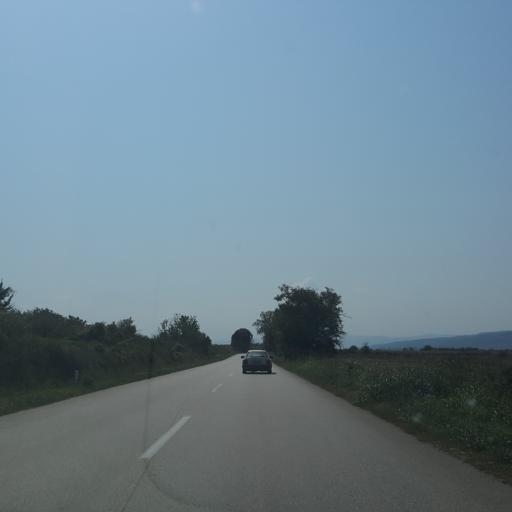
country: RS
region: Central Serbia
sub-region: Zajecarski Okrug
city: Knjazevac
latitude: 43.6766
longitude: 22.2892
